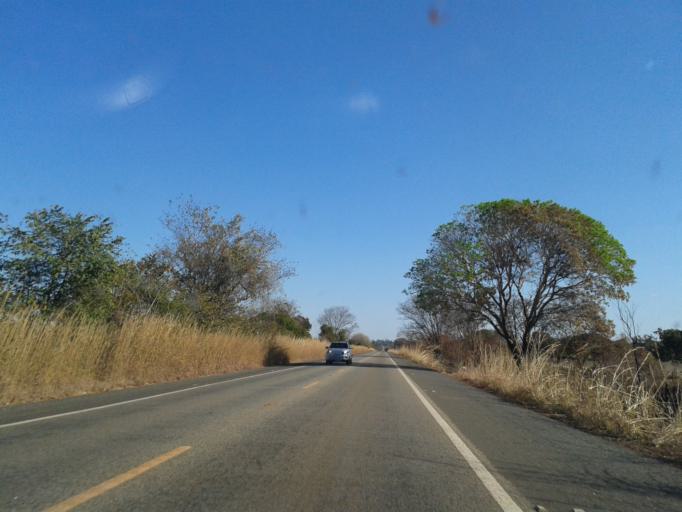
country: BR
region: Goias
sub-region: Mozarlandia
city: Mozarlandia
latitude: -15.0540
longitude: -50.6109
